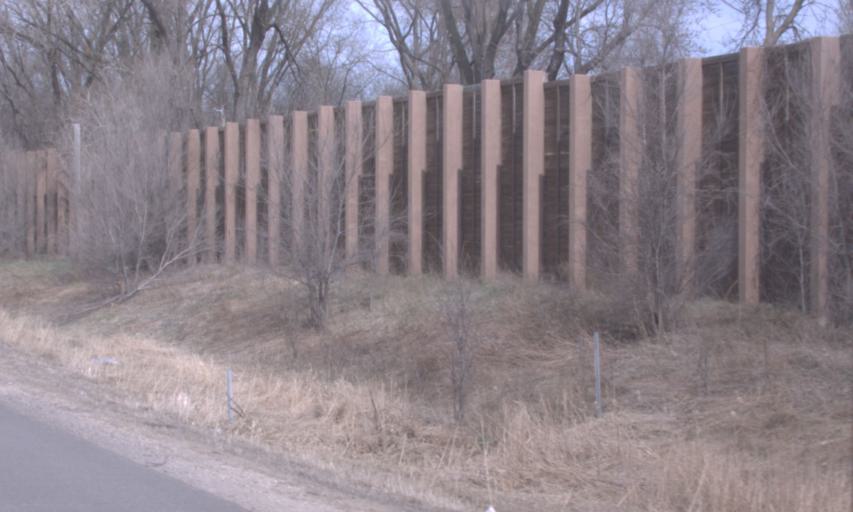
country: US
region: Minnesota
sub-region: Anoka County
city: Coon Rapids
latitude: 45.1663
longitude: -93.2887
